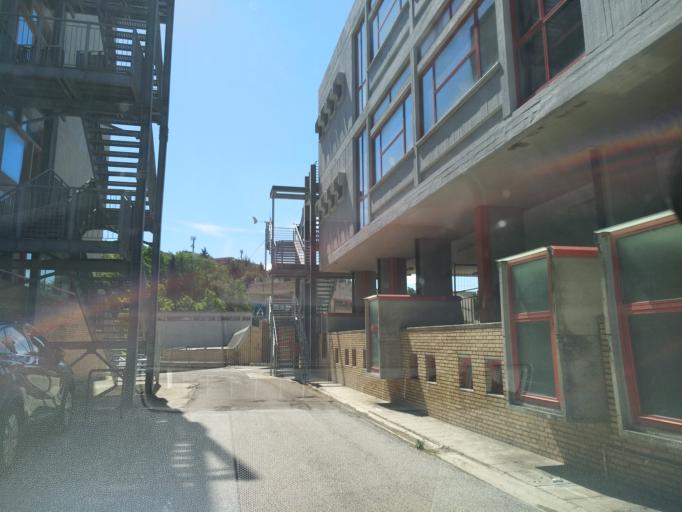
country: IT
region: The Marches
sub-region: Provincia di Pesaro e Urbino
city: Urbino
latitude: 43.7364
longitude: 12.6289
